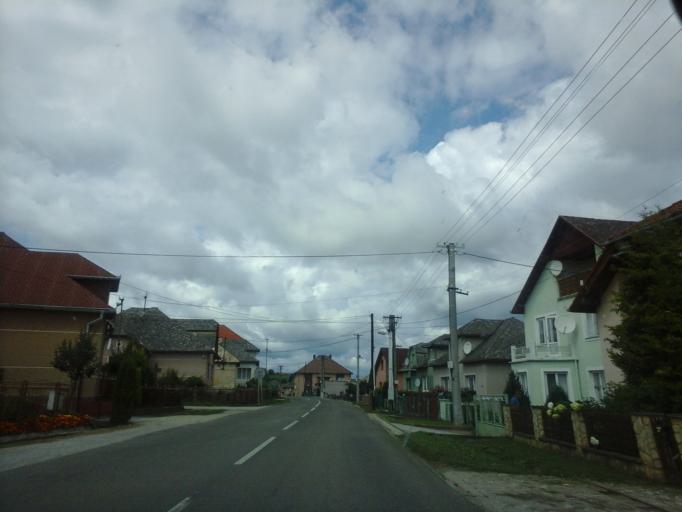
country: HU
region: Borsod-Abauj-Zemplen
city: Putnok
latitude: 48.4917
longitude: 20.4403
